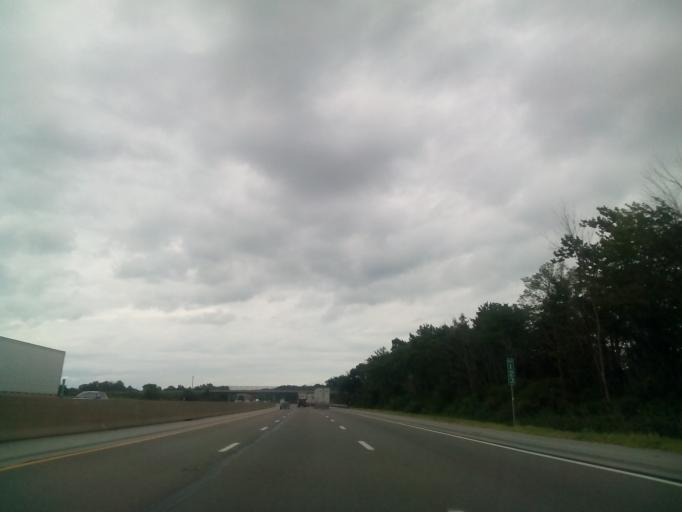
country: US
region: Ohio
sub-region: Erie County
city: Huron
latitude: 41.3257
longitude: -82.5241
